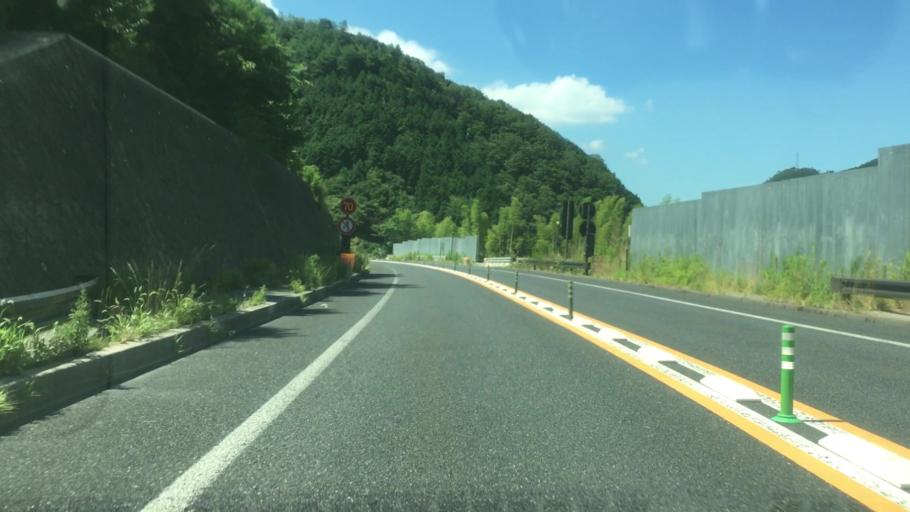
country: JP
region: Tottori
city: Tottori
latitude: 35.2997
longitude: 134.2026
